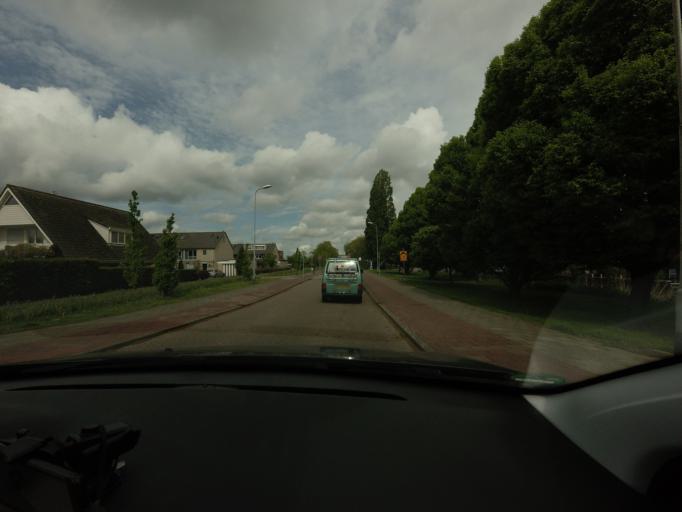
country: NL
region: North Holland
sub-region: Gemeente Zaanstad
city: Zaandam
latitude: 52.4368
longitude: 4.8704
